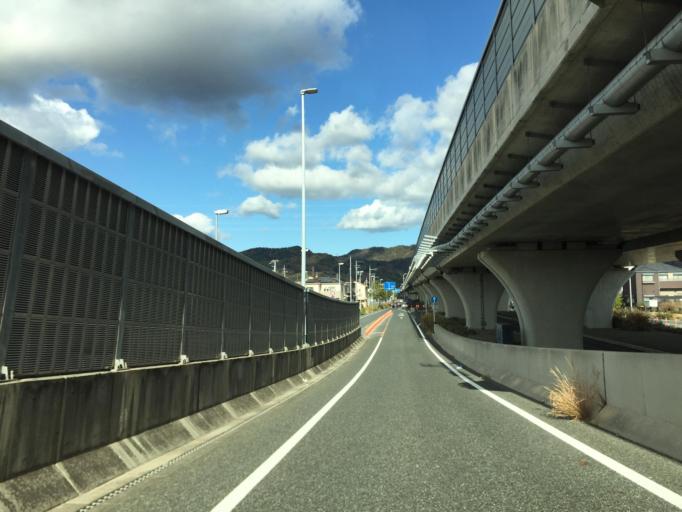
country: JP
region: Wakayama
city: Wakayama-shi
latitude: 34.2511
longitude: 135.1746
